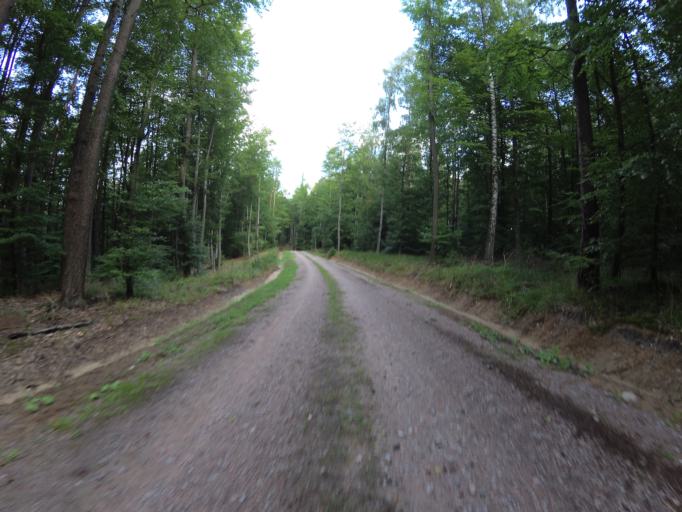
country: PL
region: Pomeranian Voivodeship
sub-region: Powiat wejherowski
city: Bojano
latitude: 54.5159
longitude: 18.4245
